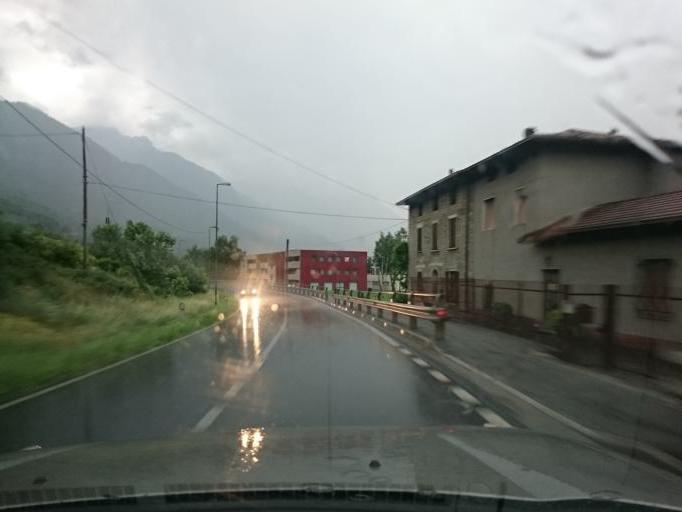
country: IT
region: Lombardy
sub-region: Provincia di Brescia
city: Capo di Ponte
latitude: 46.0220
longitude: 10.3450
